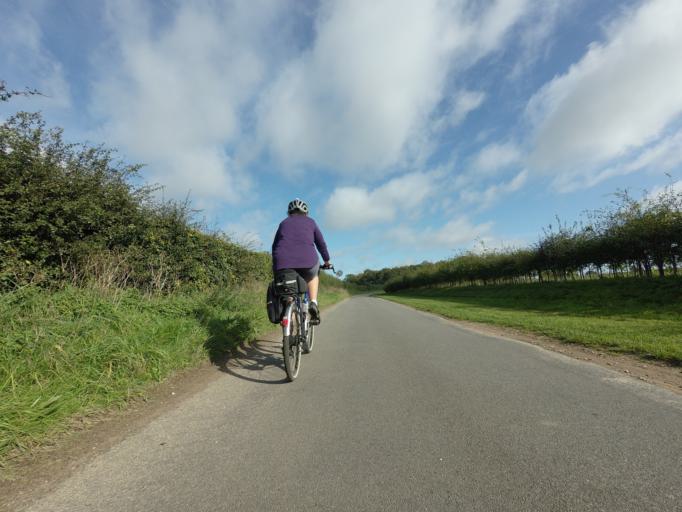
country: GB
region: England
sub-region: Norfolk
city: Fakenham
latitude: 52.8821
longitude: 0.6815
